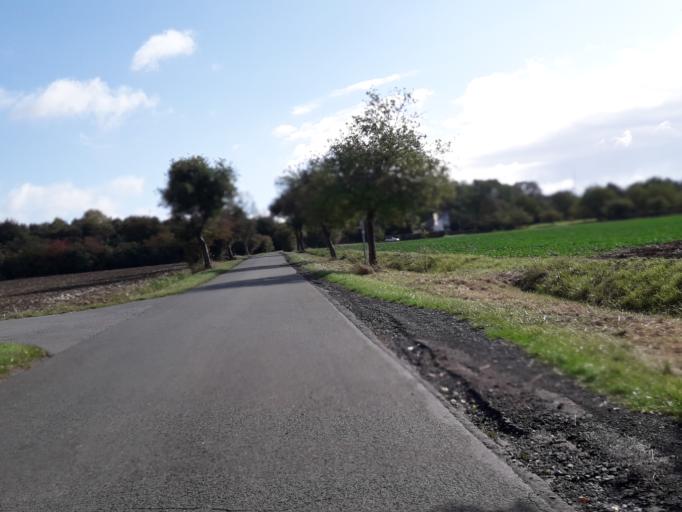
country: DE
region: North Rhine-Westphalia
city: Bad Lippspringe
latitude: 51.7397
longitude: 8.8086
